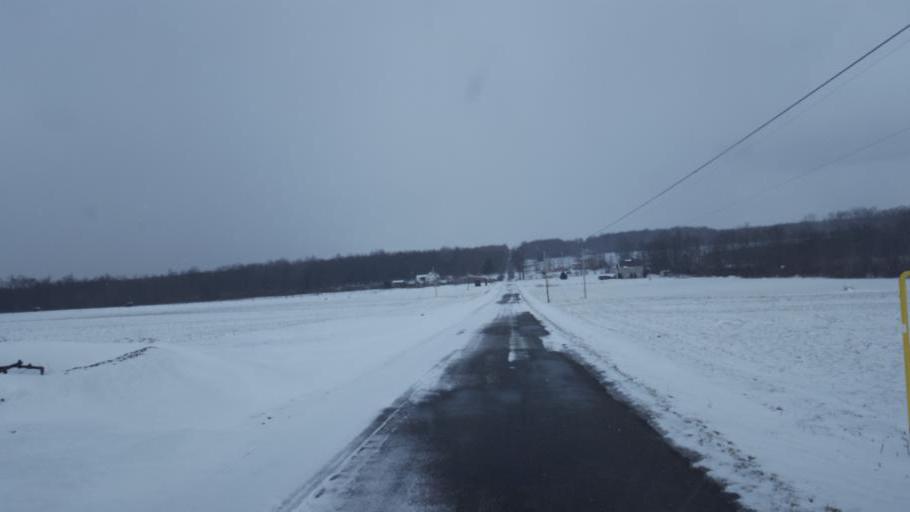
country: US
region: Pennsylvania
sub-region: Mercer County
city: Stoneboro
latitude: 41.4204
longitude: -80.0938
